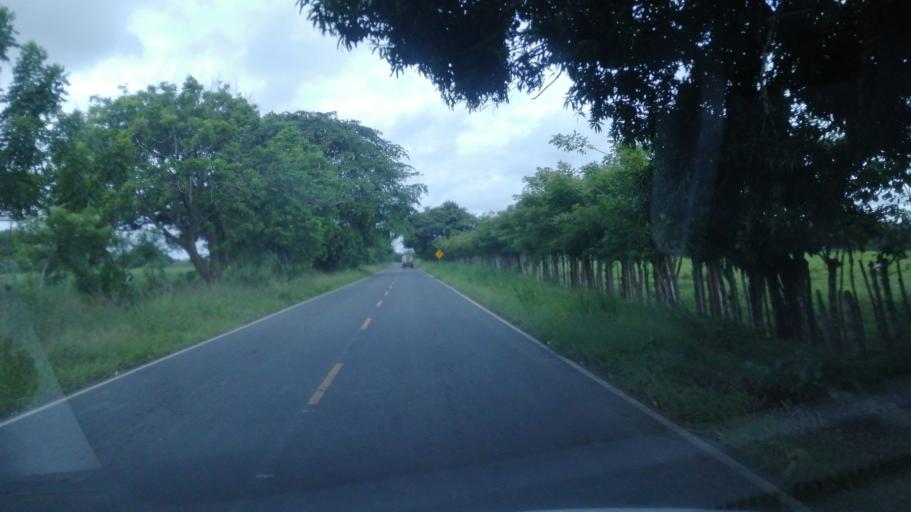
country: PA
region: Chiriqui
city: Alanje
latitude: 8.4100
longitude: -82.5158
